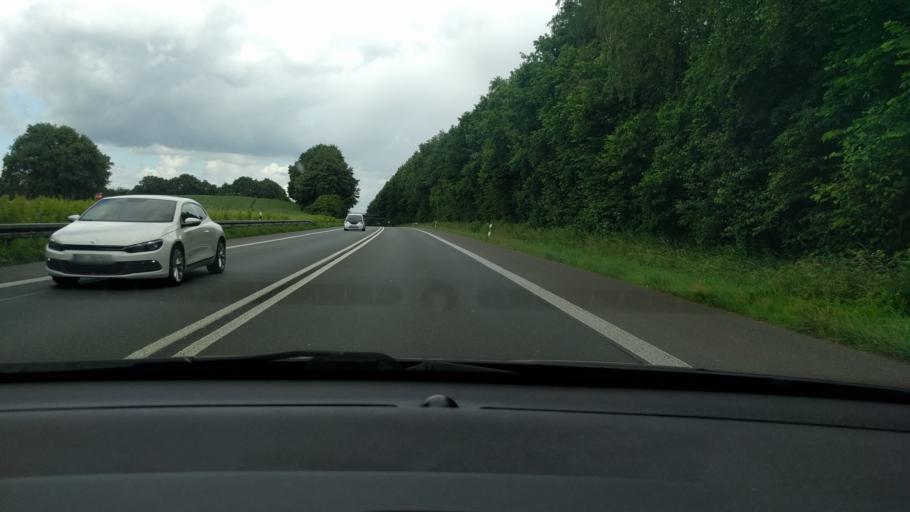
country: DE
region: North Rhine-Westphalia
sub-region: Regierungsbezirk Munster
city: Haltern
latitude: 51.7119
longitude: 7.1622
